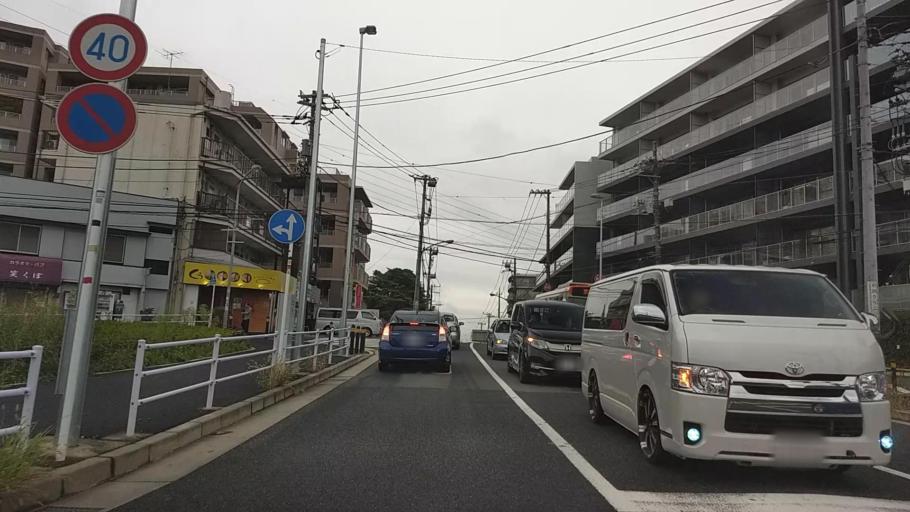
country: JP
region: Kanagawa
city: Kamakura
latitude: 35.3991
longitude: 139.5456
